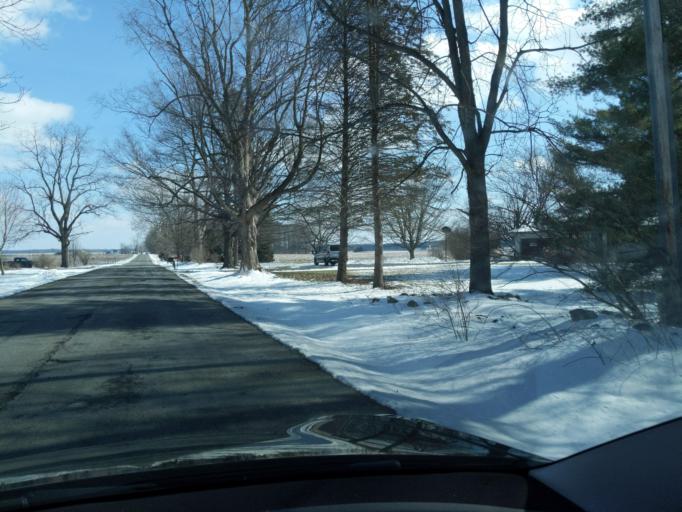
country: US
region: Michigan
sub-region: Ingham County
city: Mason
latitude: 42.6111
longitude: -84.4479
